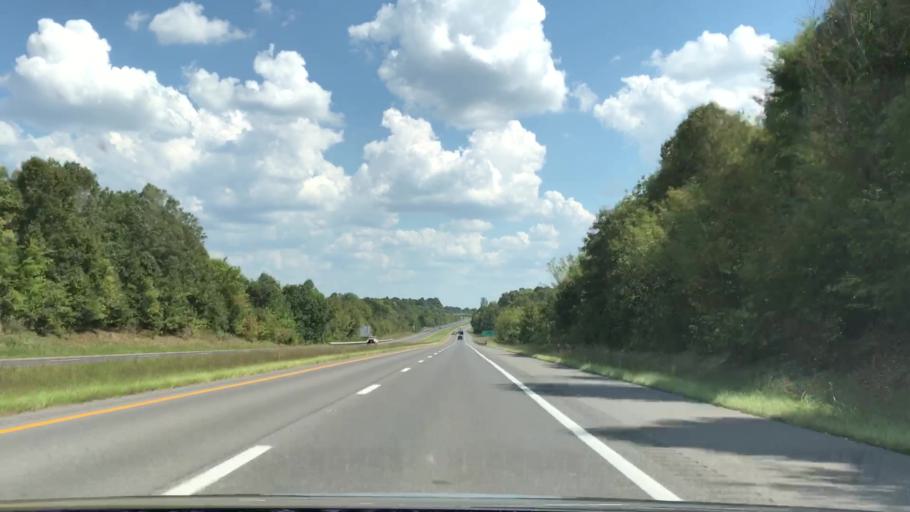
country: US
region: Kentucky
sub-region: Lyon County
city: Eddyville
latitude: 37.1094
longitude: -88.0148
